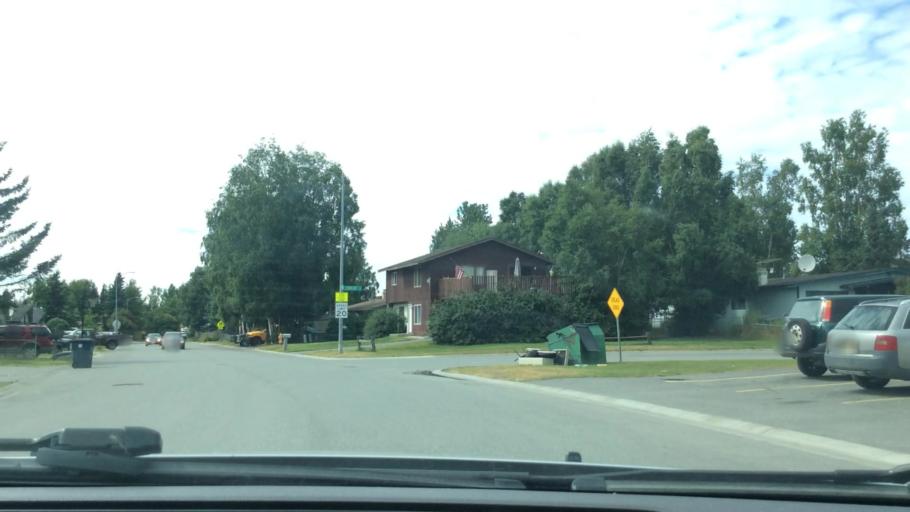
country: US
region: Alaska
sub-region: Anchorage Municipality
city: Anchorage
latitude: 61.2205
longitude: -149.7821
